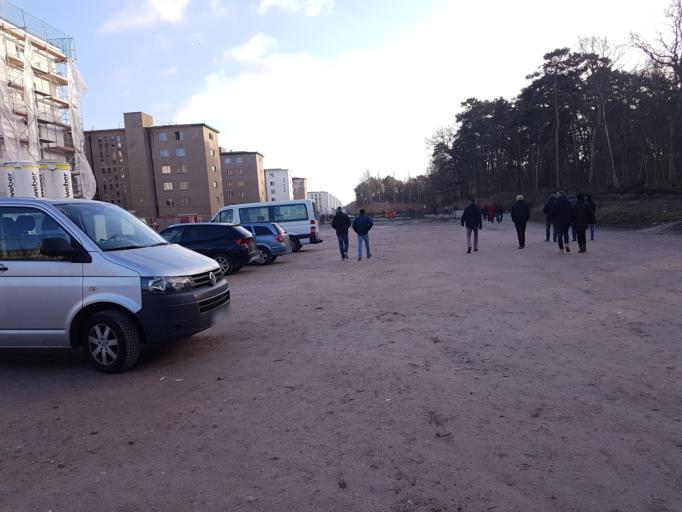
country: DE
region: Mecklenburg-Vorpommern
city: Ostseebad Binz
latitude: 54.4372
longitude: 13.5758
